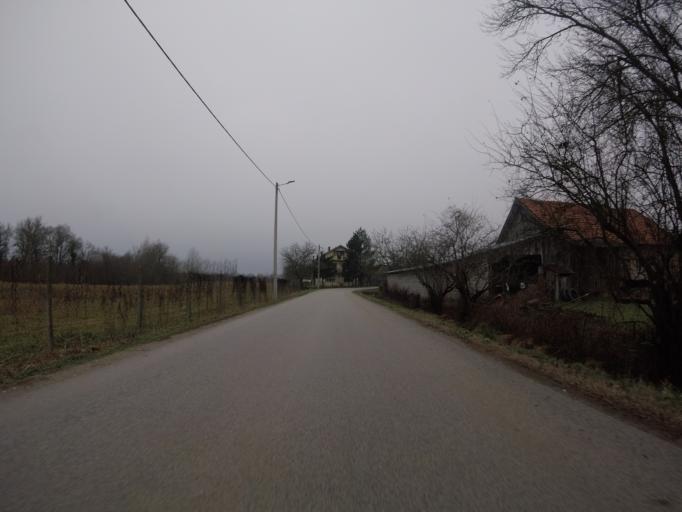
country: HR
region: Sisacko-Moslavacka
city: Lekenik
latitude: 45.6201
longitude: 16.3272
